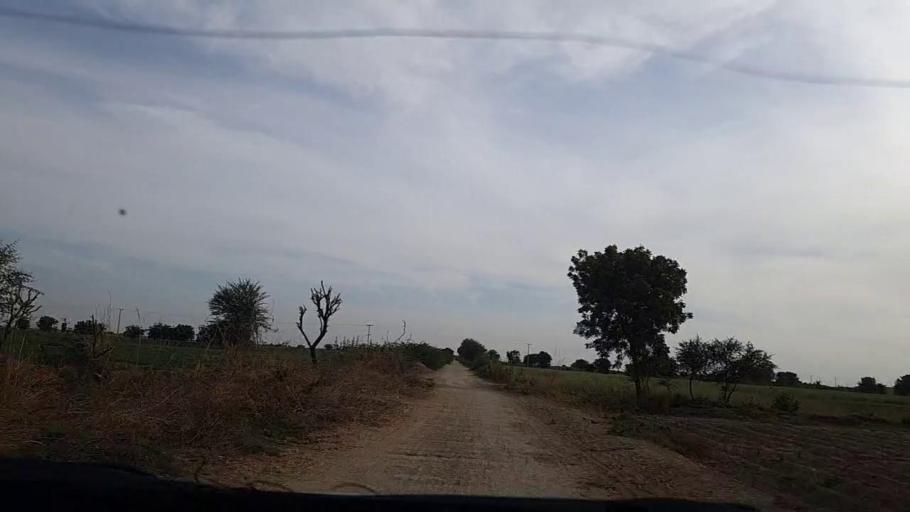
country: PK
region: Sindh
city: Dhoro Naro
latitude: 25.4059
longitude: 69.5179
